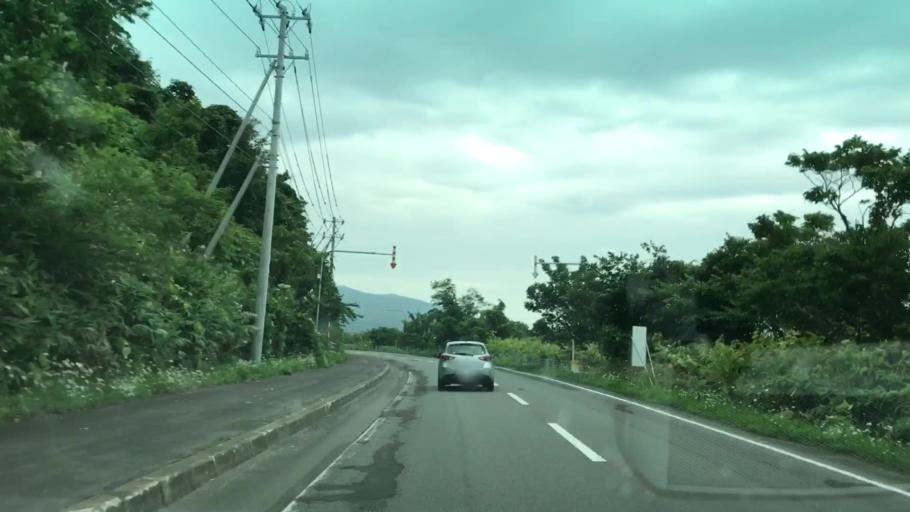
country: JP
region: Hokkaido
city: Iwanai
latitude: 42.7580
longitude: 140.2658
